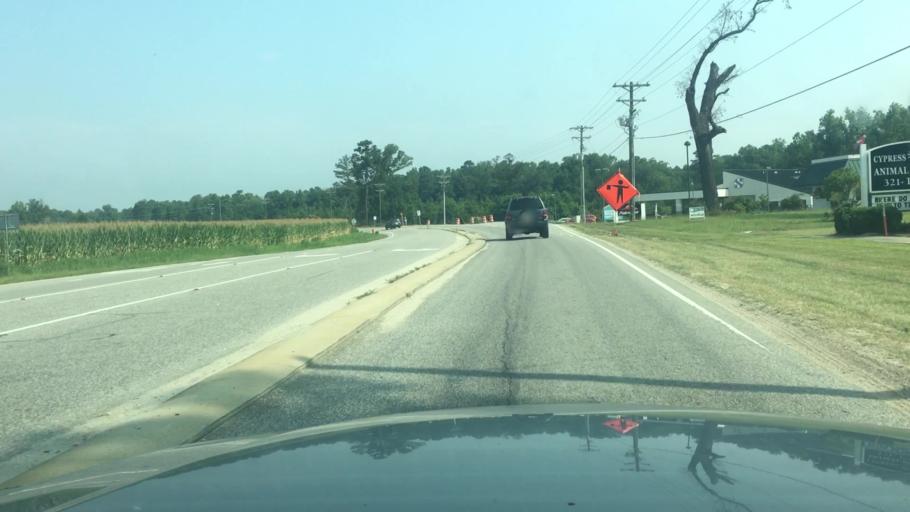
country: US
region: North Carolina
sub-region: Cumberland County
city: Hope Mills
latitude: 34.9252
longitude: -78.9101
